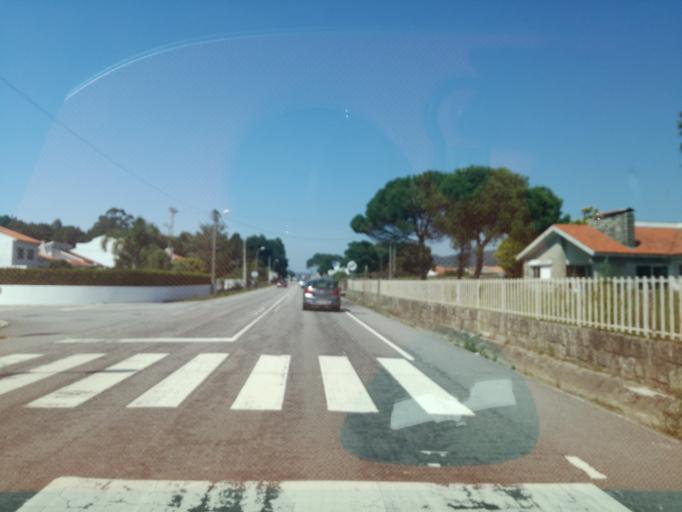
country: PT
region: Braga
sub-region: Esposende
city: Esposende
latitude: 41.5432
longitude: -8.7822
